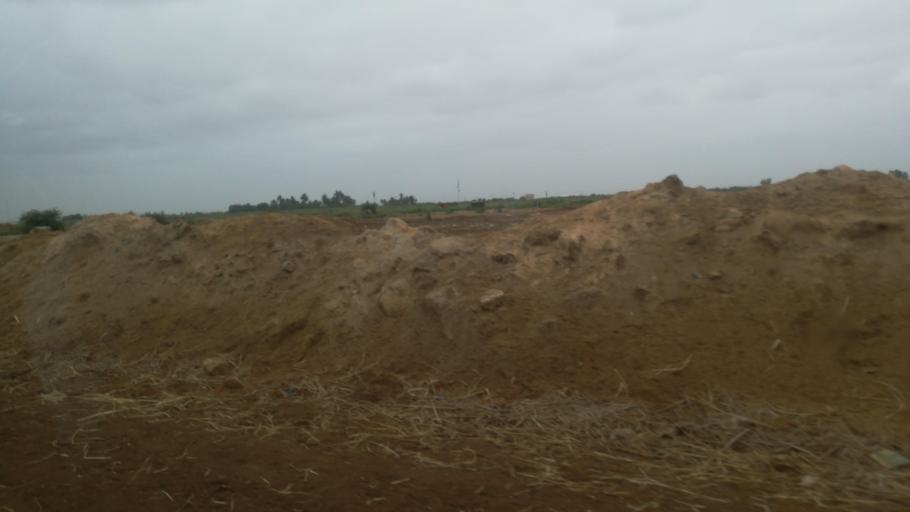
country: SN
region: Saint-Louis
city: Rosso
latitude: 16.2821
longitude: -16.1573
